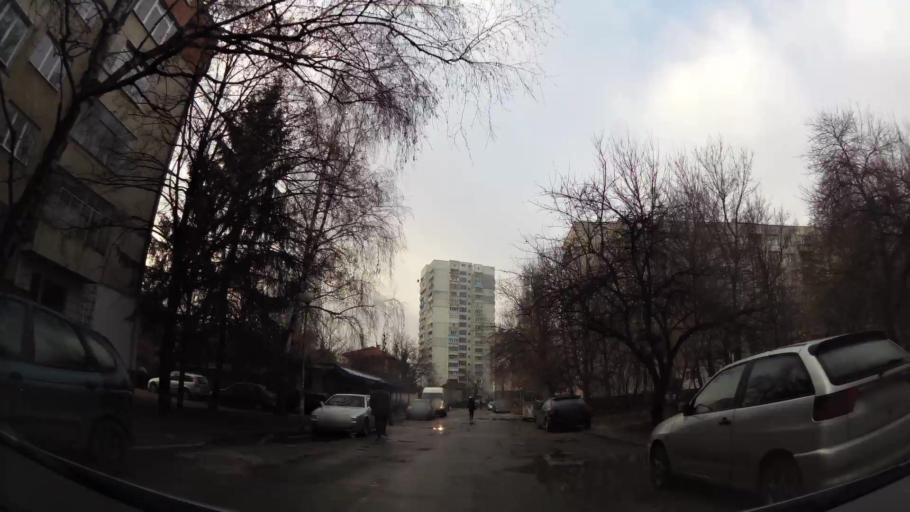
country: BG
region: Sofia-Capital
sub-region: Stolichna Obshtina
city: Sofia
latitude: 42.7255
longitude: 23.3087
